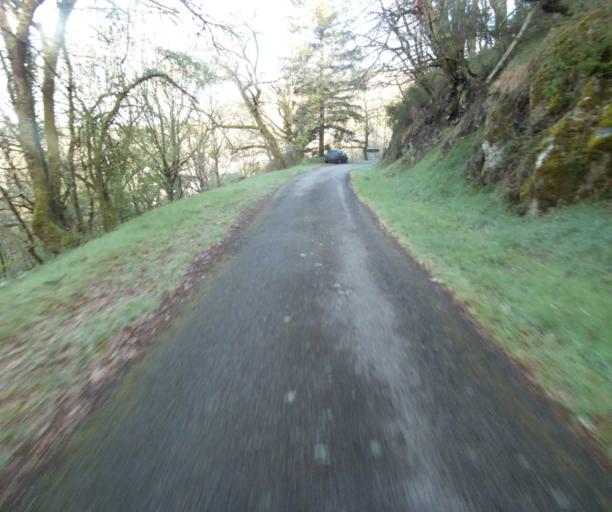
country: FR
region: Limousin
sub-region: Departement de la Correze
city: Correze
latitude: 45.2986
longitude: 1.8535
